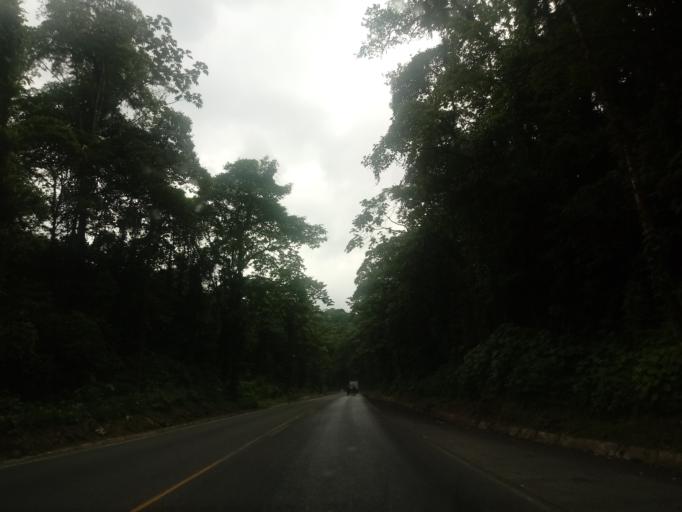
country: CR
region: San Jose
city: Dulce Nombre de Jesus
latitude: 10.1533
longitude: -83.9411
